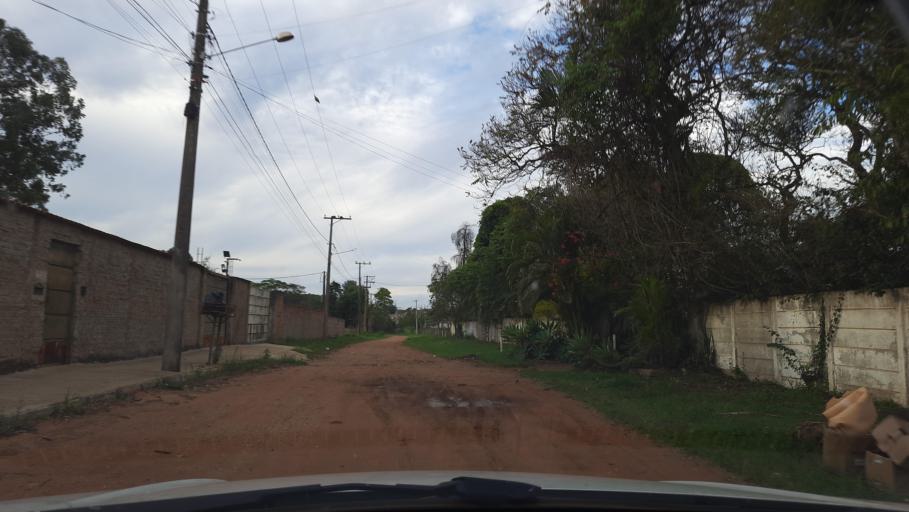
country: BR
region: Sao Paulo
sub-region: Casa Branca
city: Casa Branca
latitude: -21.7779
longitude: -47.0651
